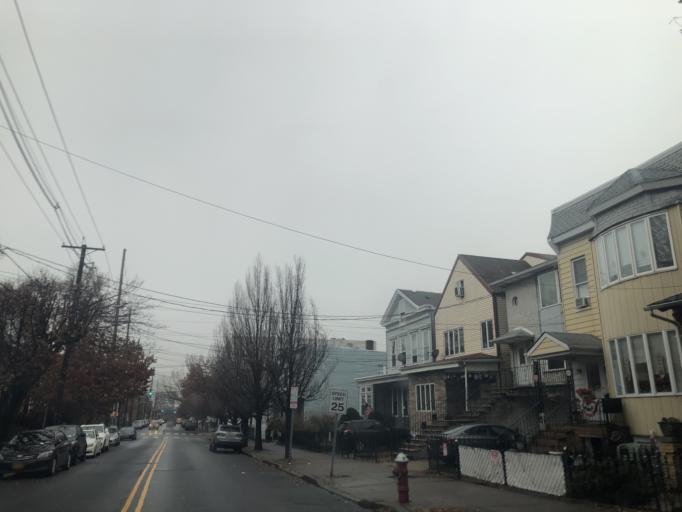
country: US
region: New Jersey
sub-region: Hudson County
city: Hoboken
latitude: 40.7448
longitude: -74.0532
